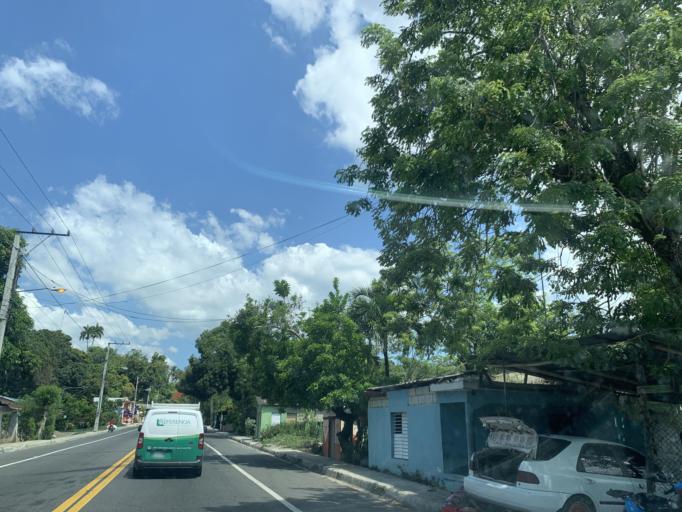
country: DO
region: Puerto Plata
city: Altamira
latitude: 19.6838
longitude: -70.8399
